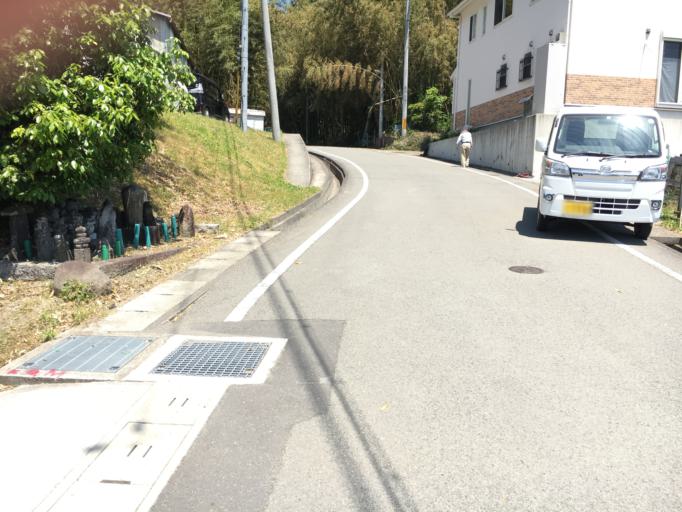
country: JP
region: Kyoto
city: Kameoka
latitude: 35.0253
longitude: 135.5931
